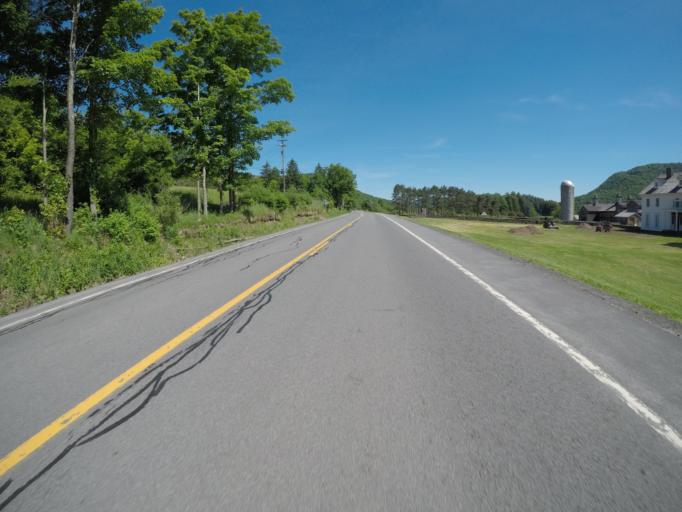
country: US
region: New York
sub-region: Delaware County
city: Delhi
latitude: 42.2241
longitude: -74.9691
